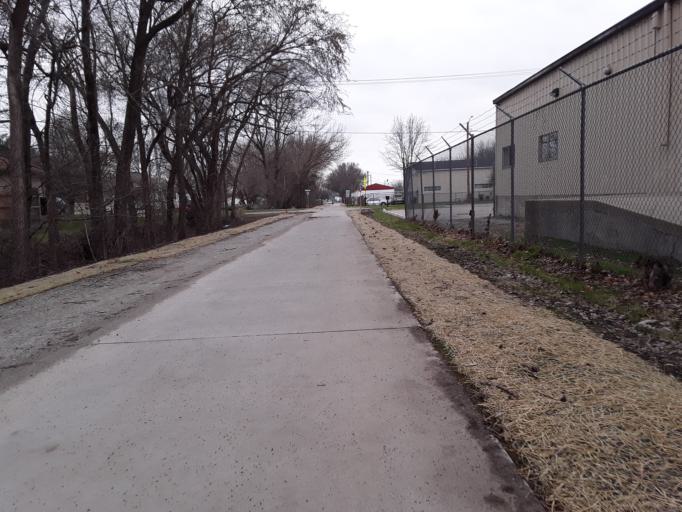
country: US
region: Nebraska
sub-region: Lancaster County
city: Lincoln
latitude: 40.8514
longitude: -96.6337
